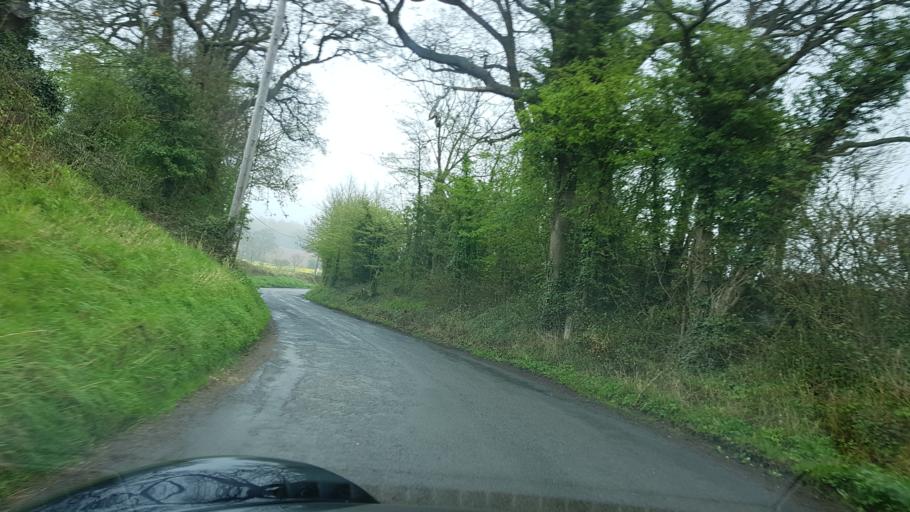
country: GB
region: England
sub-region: Herefordshire
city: Yatton
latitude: 52.0017
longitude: -2.5185
